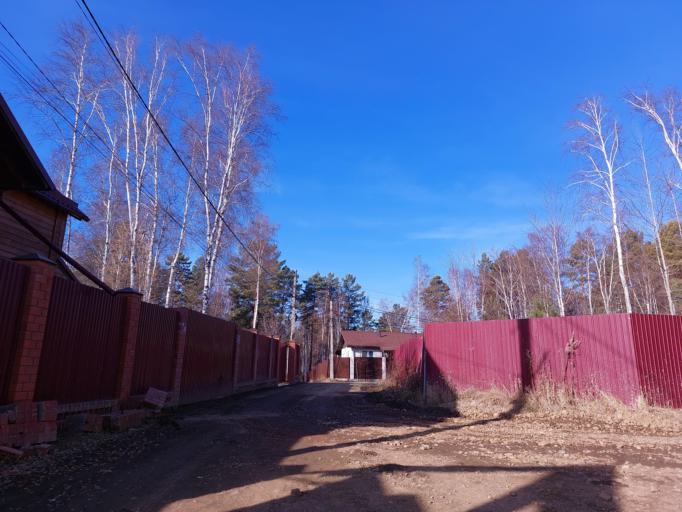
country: RU
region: Irkutsk
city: Pivovarikha
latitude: 52.1873
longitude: 104.4547
